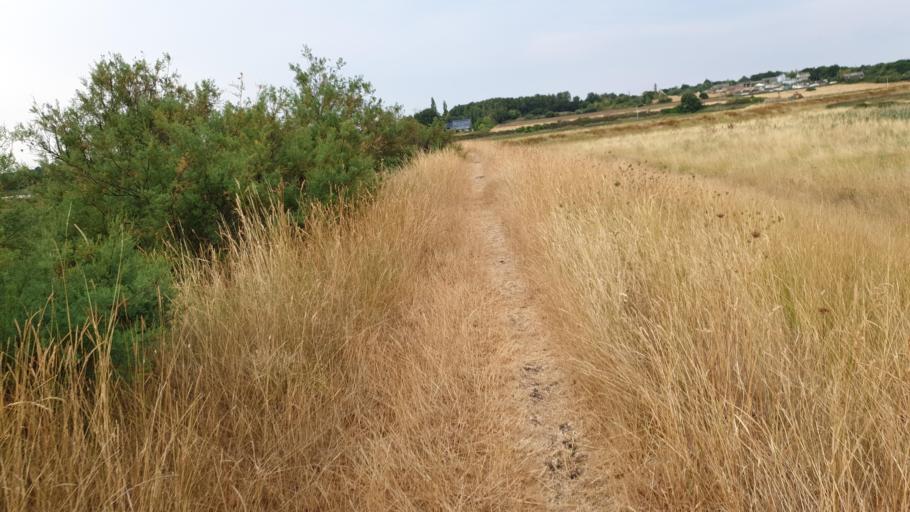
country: GB
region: England
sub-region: Essex
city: Alresford
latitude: 51.8350
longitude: 0.9881
